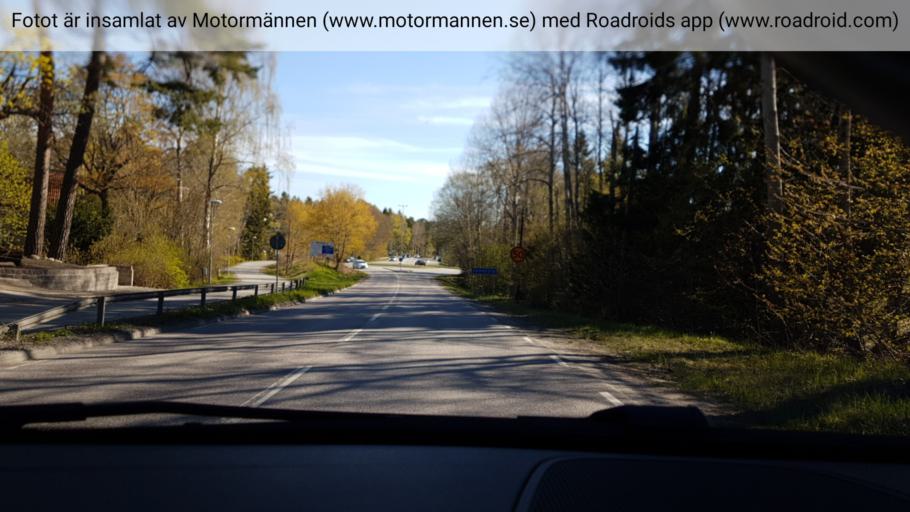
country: SE
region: Stockholm
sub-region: Varmdo Kommun
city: Hemmesta
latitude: 59.3202
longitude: 18.4793
